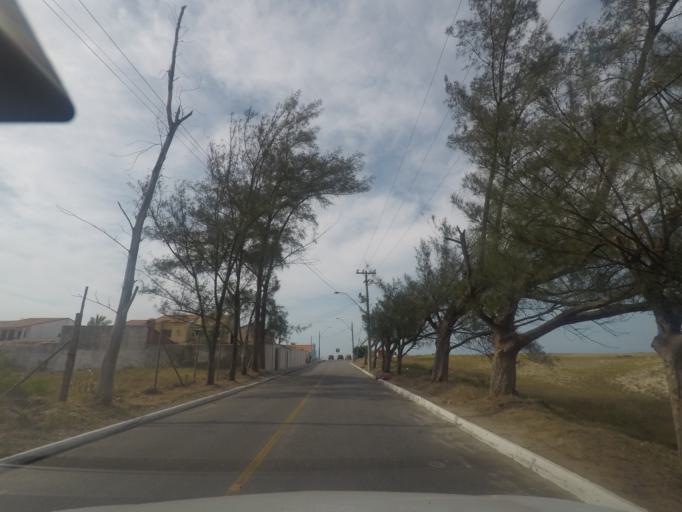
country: BR
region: Rio de Janeiro
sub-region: Marica
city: Marica
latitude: -22.9606
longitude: -42.8275
